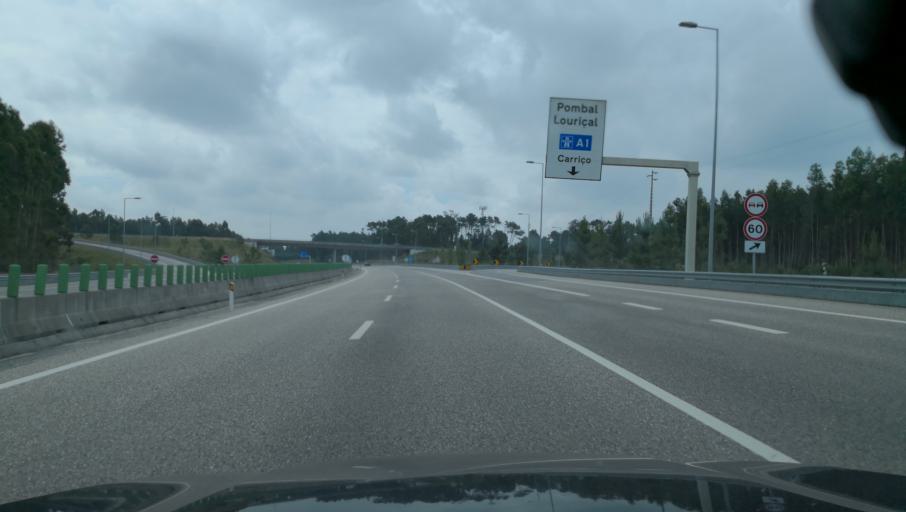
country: PT
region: Leiria
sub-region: Pombal
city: Lourical
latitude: 39.9916
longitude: -8.7971
